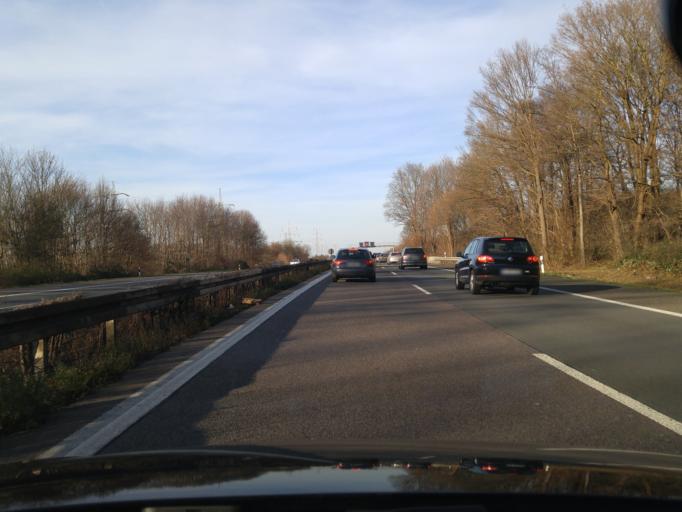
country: DE
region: North Rhine-Westphalia
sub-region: Regierungsbezirk Koln
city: Ostheim
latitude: 50.9248
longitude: 7.0595
